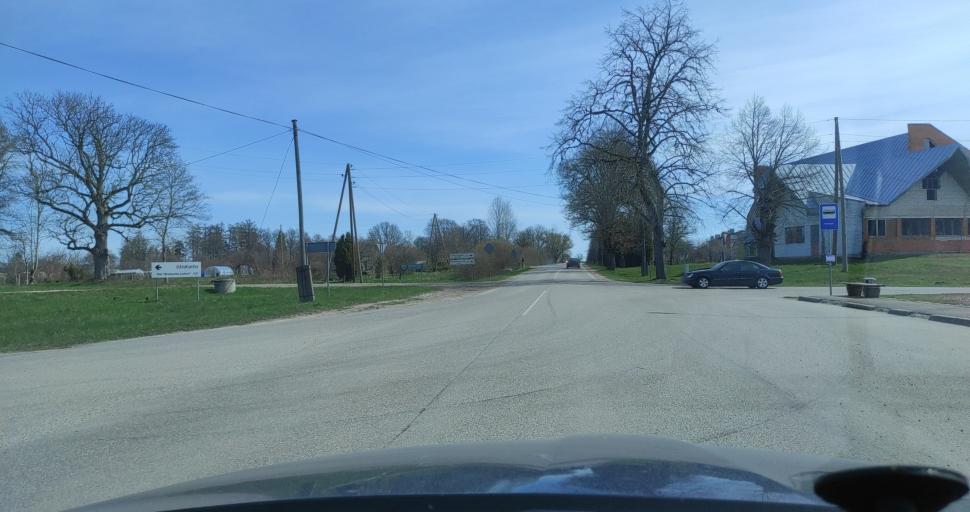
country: LV
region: Talsu Rajons
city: Talsi
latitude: 57.2260
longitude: 22.5201
